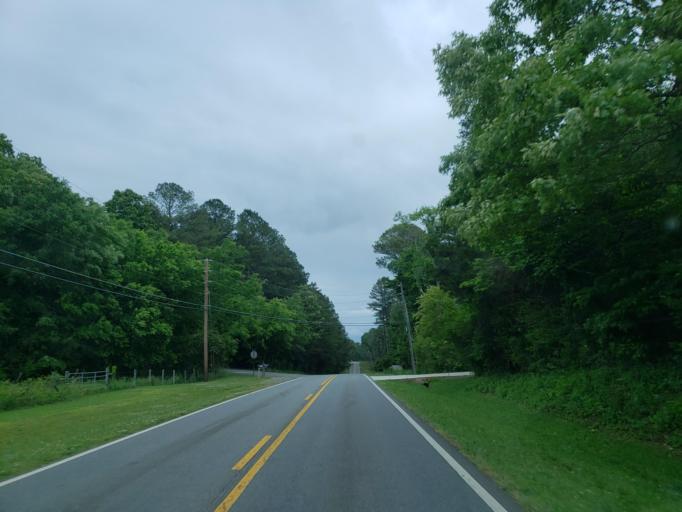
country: US
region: Georgia
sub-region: Bartow County
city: Euharlee
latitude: 34.1757
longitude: -84.9938
